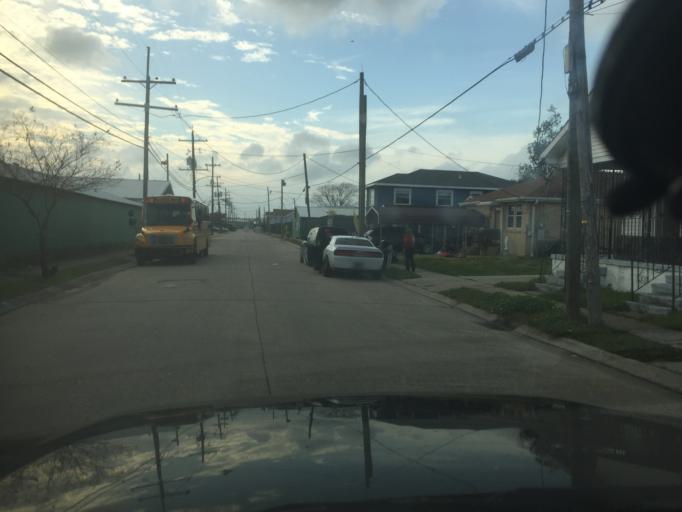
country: US
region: Louisiana
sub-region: Orleans Parish
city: New Orleans
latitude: 29.9860
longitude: -90.0802
